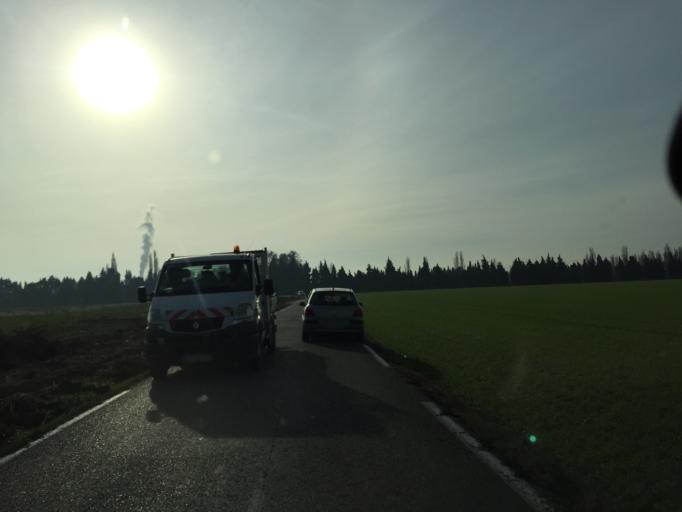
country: FR
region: Provence-Alpes-Cote d'Azur
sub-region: Departement du Vaucluse
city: Orange
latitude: 44.1392
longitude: 4.8412
